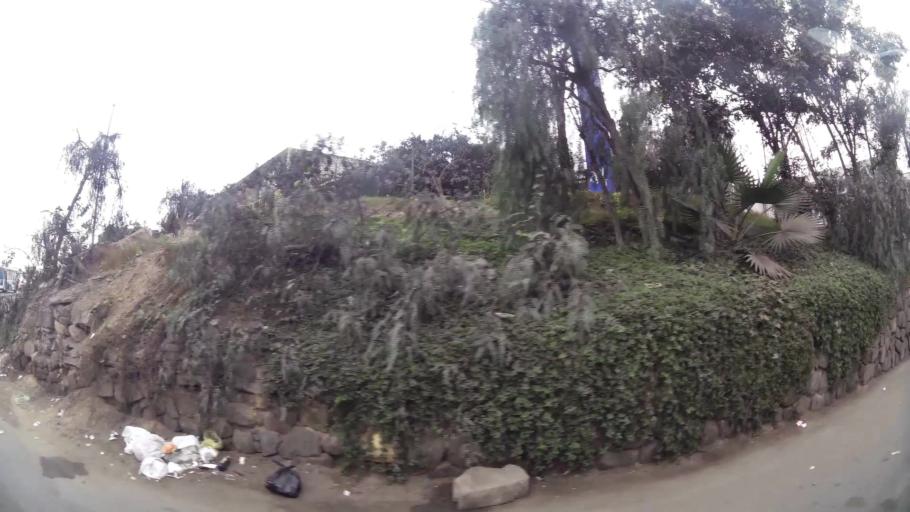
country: PE
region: Lima
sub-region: Lima
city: Surco
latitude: -12.1731
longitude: -76.9782
